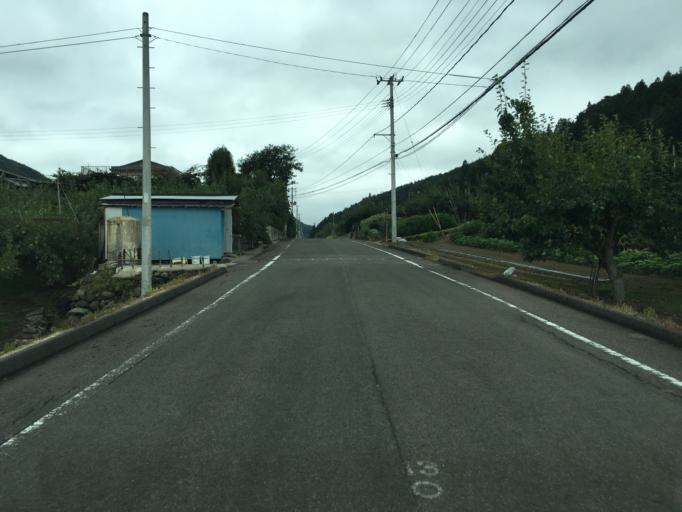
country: JP
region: Fukushima
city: Fukushima-shi
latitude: 37.7941
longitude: 140.3894
